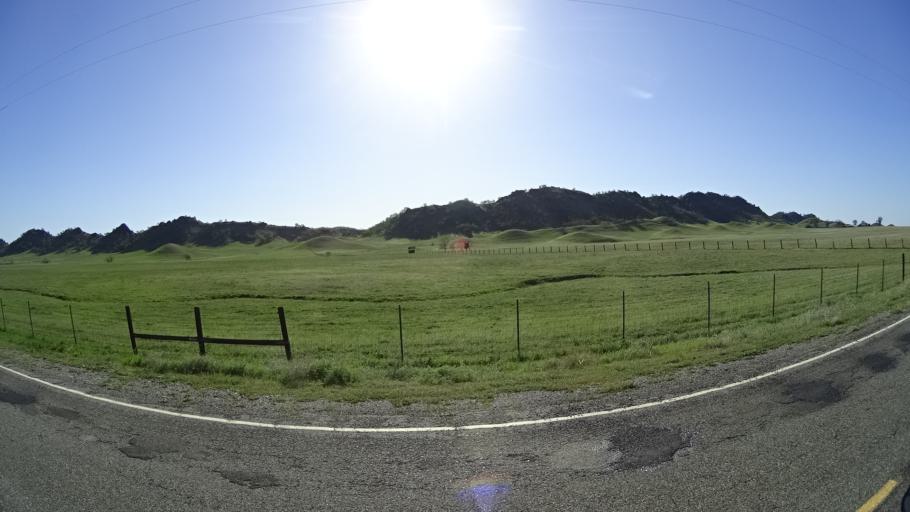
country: US
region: California
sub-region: Tehama County
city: Rancho Tehama Reserve
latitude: 39.7383
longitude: -122.5475
